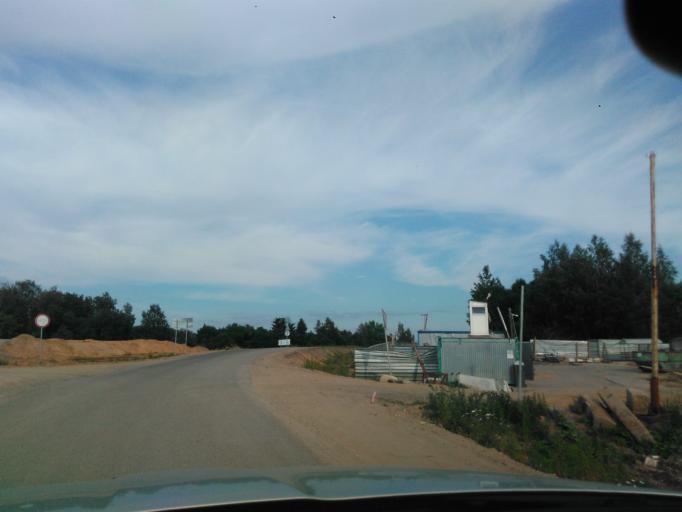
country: RU
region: Moskovskaya
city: Mendeleyevo
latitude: 56.1072
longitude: 37.2473
